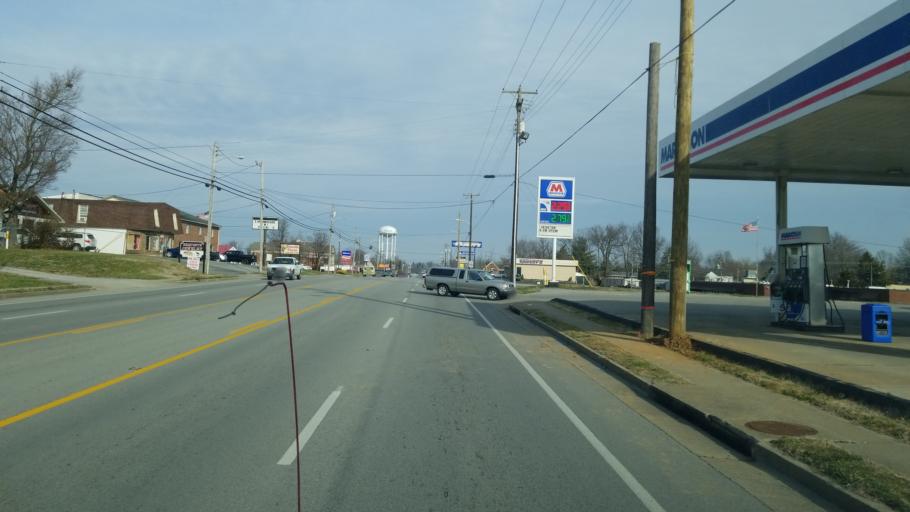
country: US
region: Kentucky
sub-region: Boyle County
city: Danville
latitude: 37.6259
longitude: -84.7747
